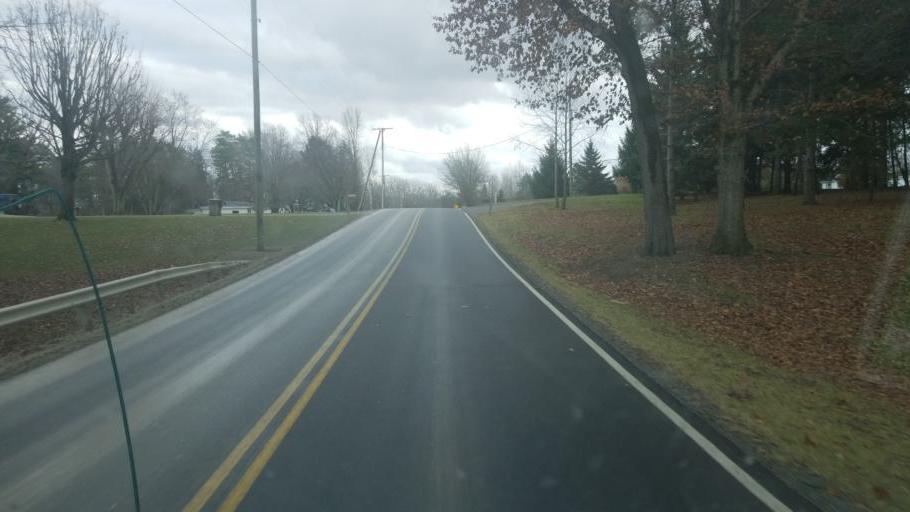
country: US
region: Ohio
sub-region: Wyandot County
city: Upper Sandusky
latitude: 40.7819
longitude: -83.2396
